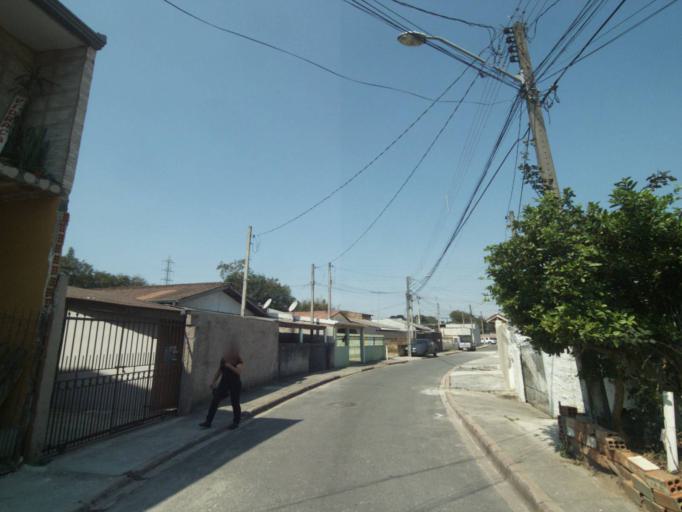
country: BR
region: Parana
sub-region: Curitiba
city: Curitiba
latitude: -25.4781
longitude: -49.3201
